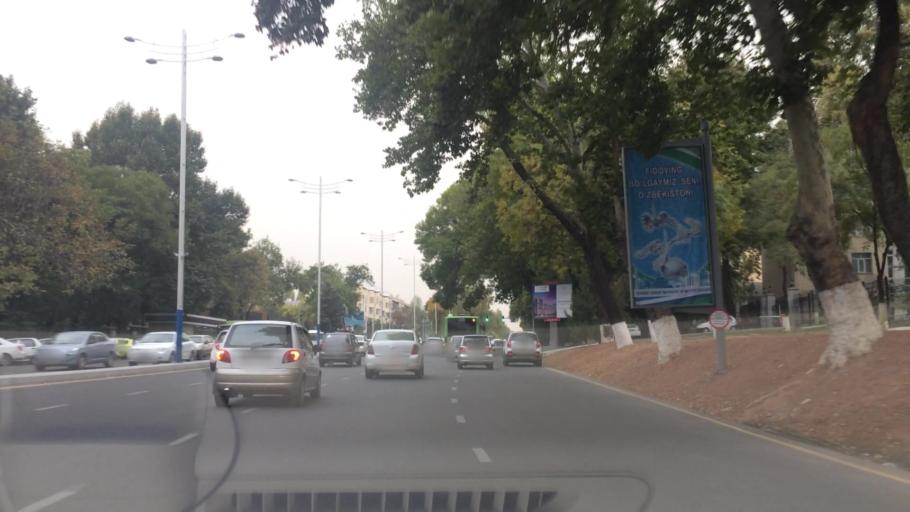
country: UZ
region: Toshkent Shahri
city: Tashkent
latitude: 41.3071
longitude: 69.2945
